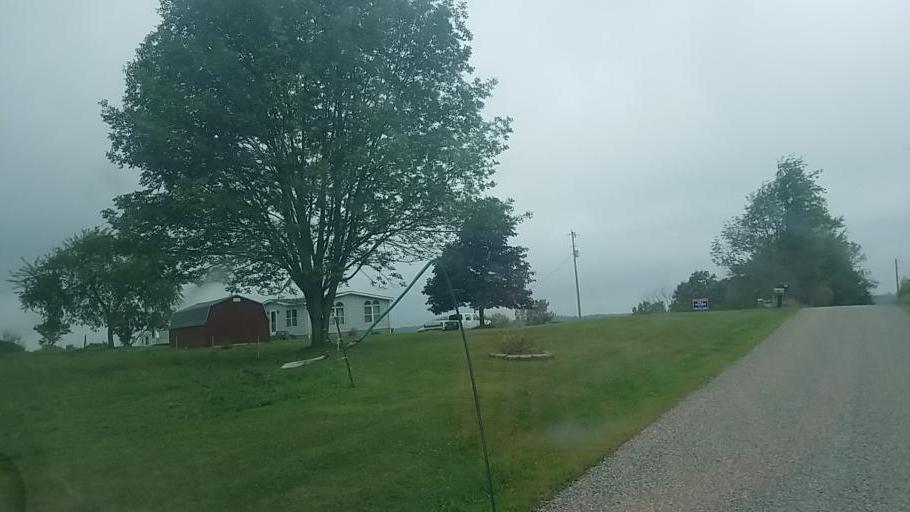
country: US
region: Ohio
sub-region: Knox County
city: Oak Hill
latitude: 40.4955
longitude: -82.1280
